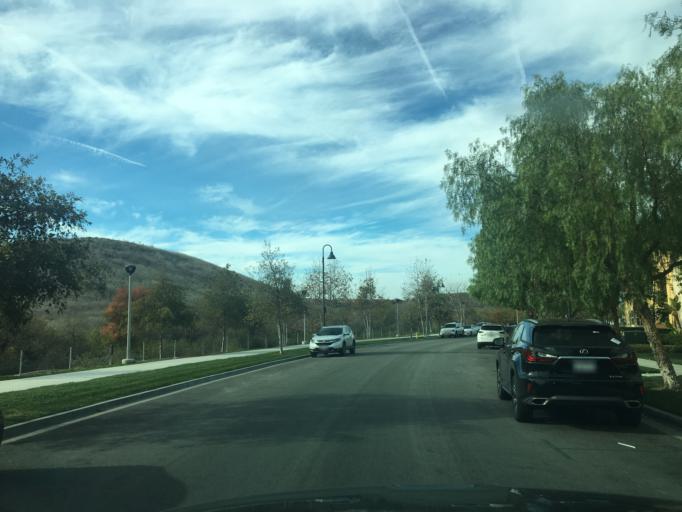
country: US
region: California
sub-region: Orange County
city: Laguna Woods
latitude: 33.6428
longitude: -117.7514
